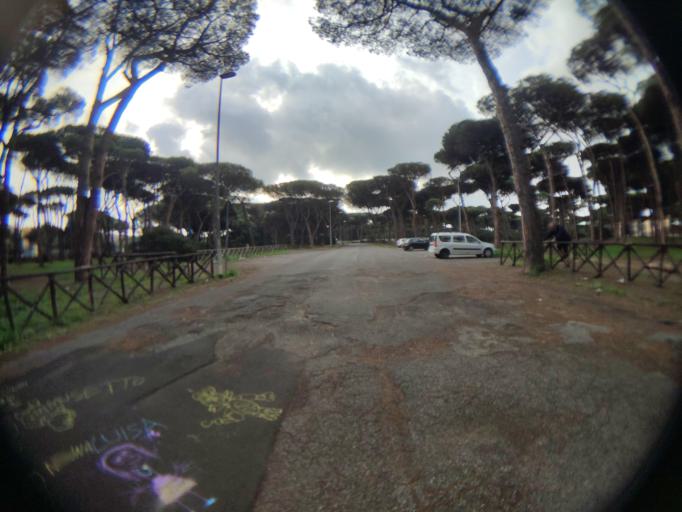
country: IT
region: Latium
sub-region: Citta metropolitana di Roma Capitale
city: Lido di Ostia
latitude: 41.7320
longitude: 12.2984
